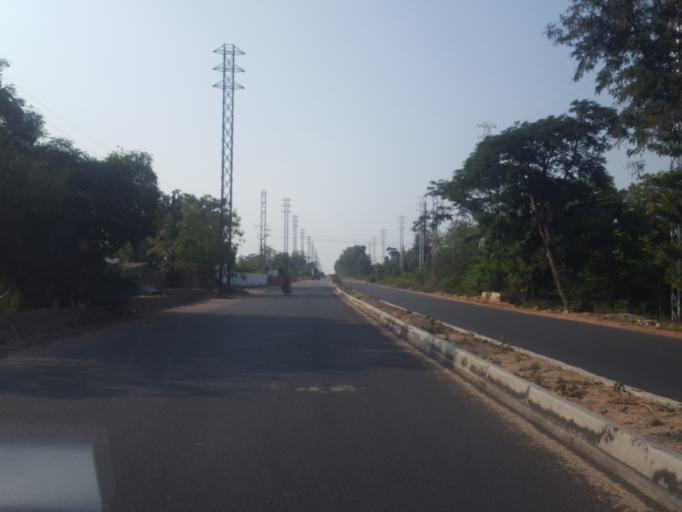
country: IN
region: Telangana
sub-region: Medak
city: Serilingampalle
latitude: 17.4056
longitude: 78.2834
